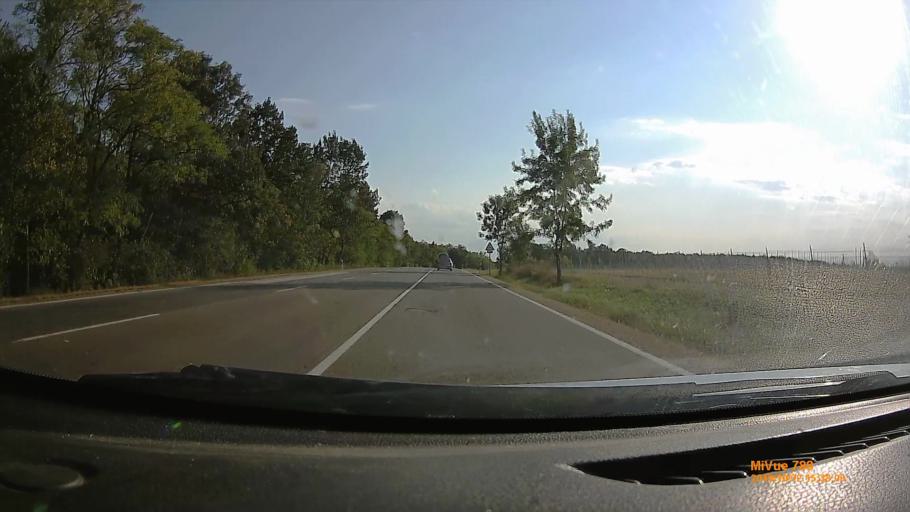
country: HU
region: Heves
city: Kerecsend
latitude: 47.8334
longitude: 20.3574
